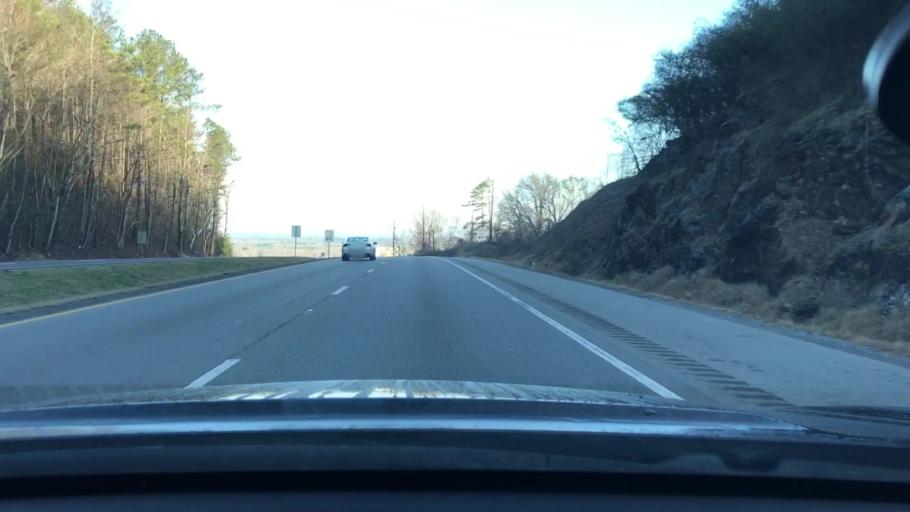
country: US
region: Alabama
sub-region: Talladega County
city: Mignon
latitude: 33.2009
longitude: -86.3074
